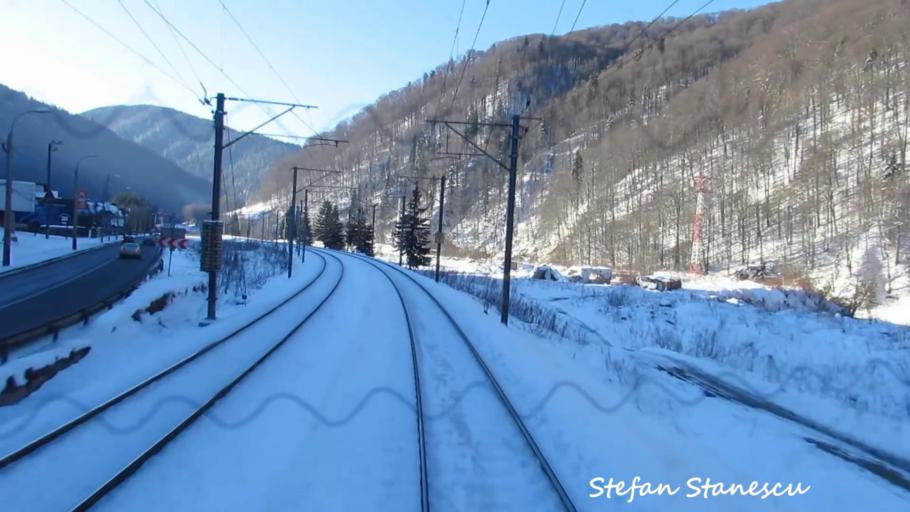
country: RO
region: Prahova
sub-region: Oras Azuga
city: Azuga
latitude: 45.4292
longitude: 25.5537
